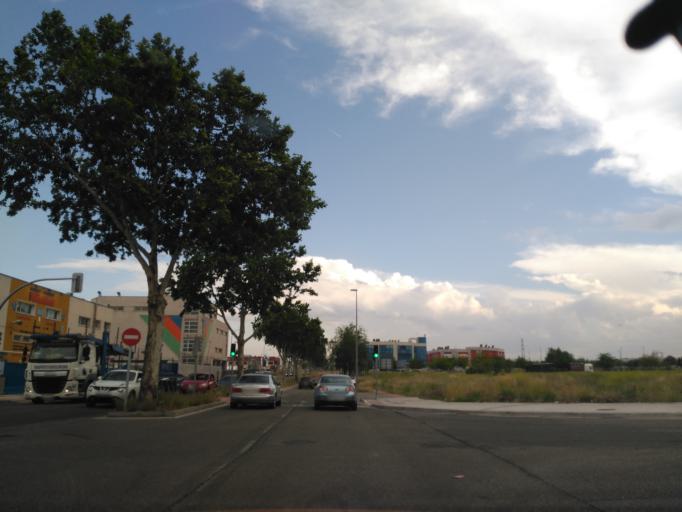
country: ES
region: Madrid
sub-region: Provincia de Madrid
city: Villaverde
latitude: 40.3378
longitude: -3.7154
